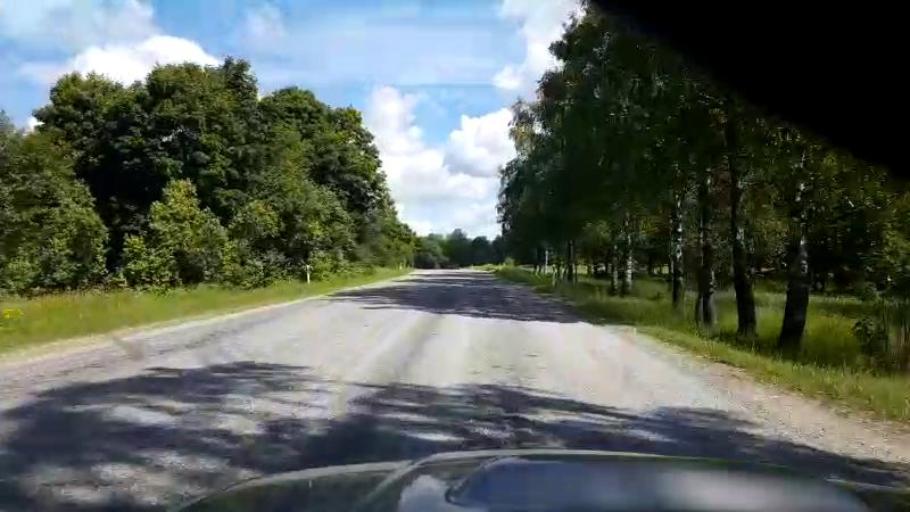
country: EE
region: Laeaene-Virumaa
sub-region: Tapa vald
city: Tapa
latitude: 59.2444
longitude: 25.9296
